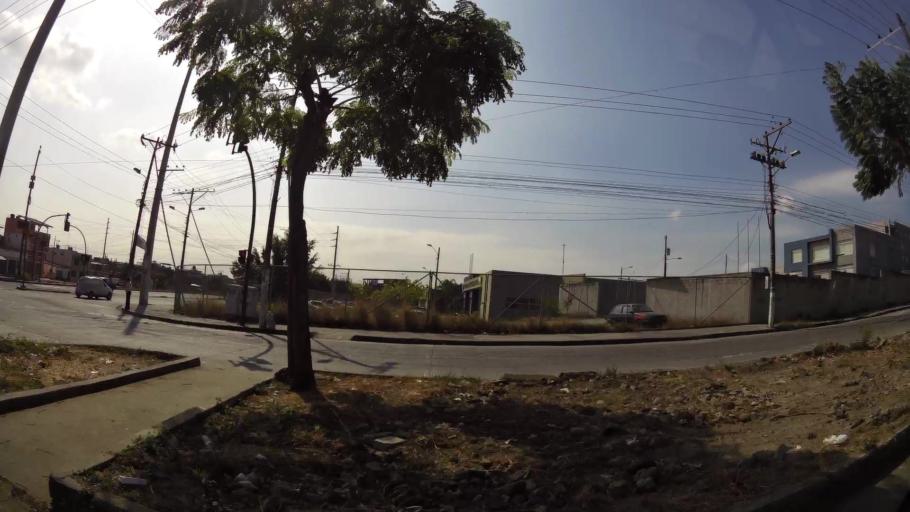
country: EC
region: Guayas
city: Eloy Alfaro
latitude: -2.1715
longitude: -79.8062
